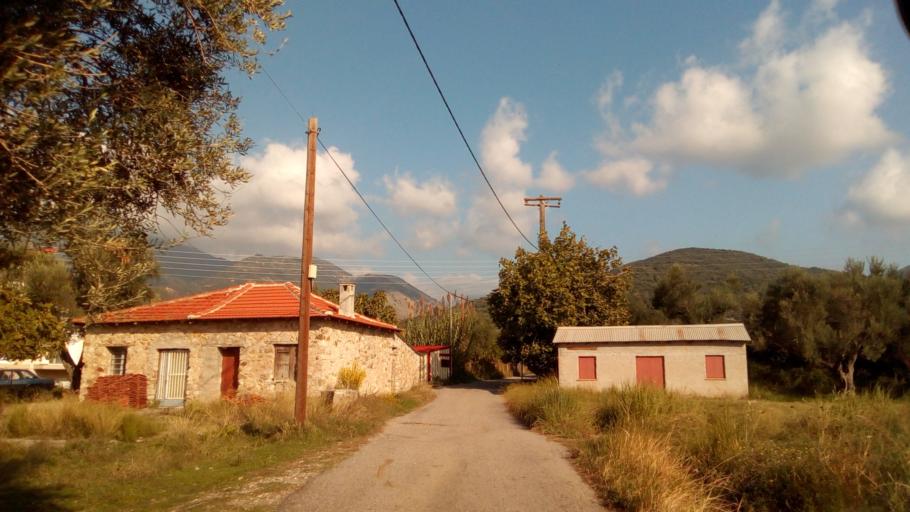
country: GR
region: West Greece
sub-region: Nomos Aitolias kai Akarnanias
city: Nafpaktos
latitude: 38.4125
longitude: 21.8890
